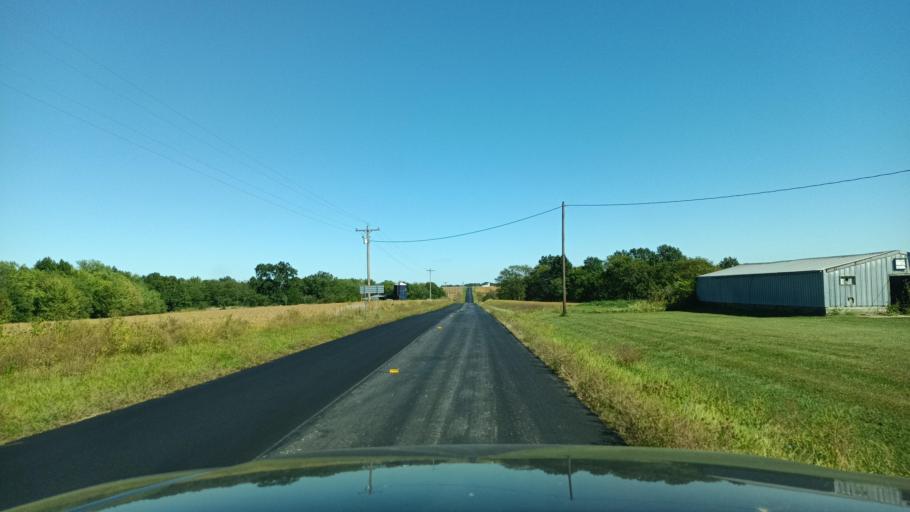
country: US
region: Missouri
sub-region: Macon County
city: La Plata
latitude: 39.9280
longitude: -92.5684
